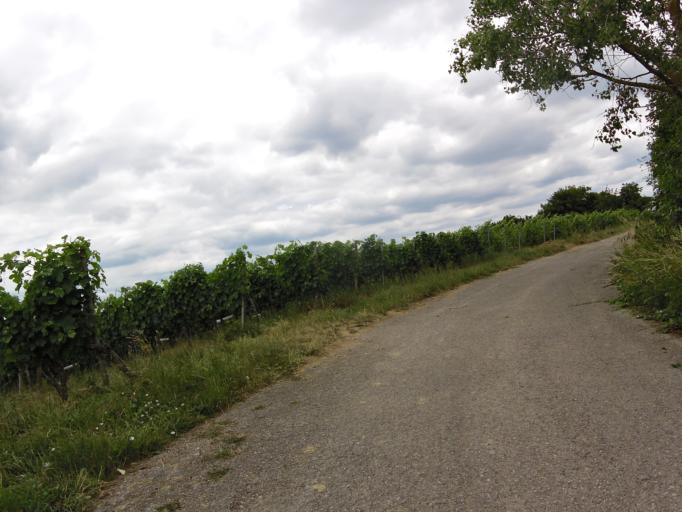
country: DE
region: Bavaria
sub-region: Regierungsbezirk Unterfranken
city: Randersacker
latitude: 49.7684
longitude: 9.9654
